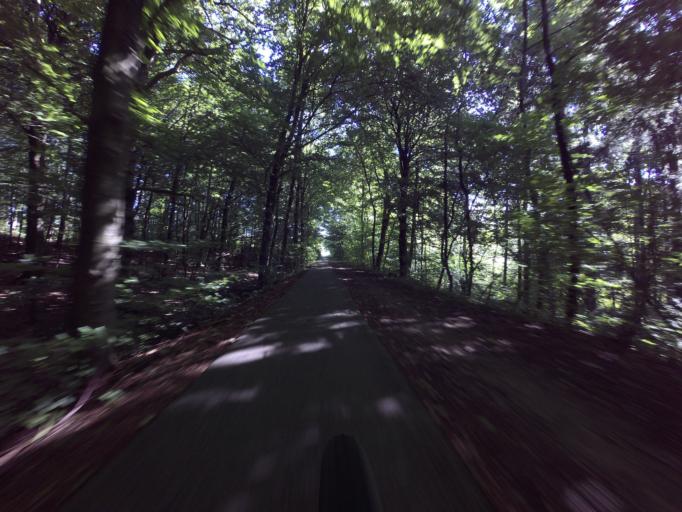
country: DK
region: Central Jutland
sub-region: Horsens Kommune
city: Braedstrup
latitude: 55.9728
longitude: 9.6249
